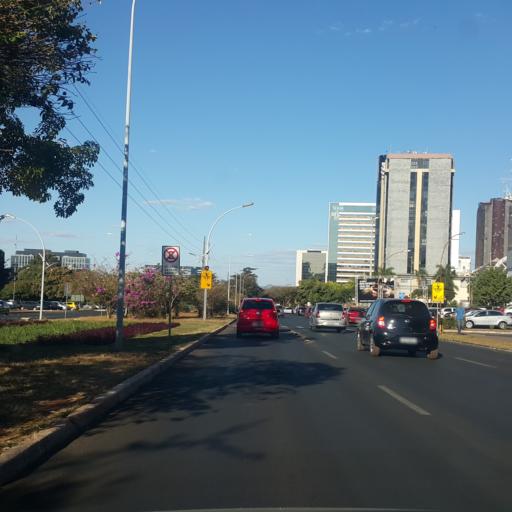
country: BR
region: Federal District
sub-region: Brasilia
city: Brasilia
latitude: -15.7859
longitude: -47.8865
